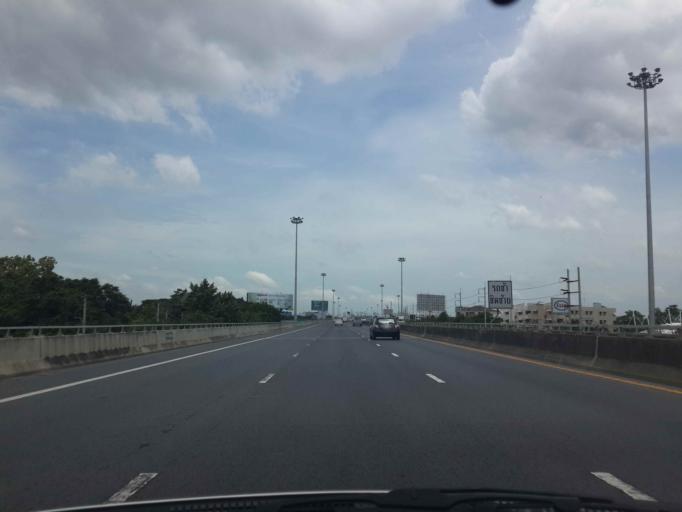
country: TH
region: Bangkok
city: Lat Phrao
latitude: 13.8222
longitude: 100.6267
